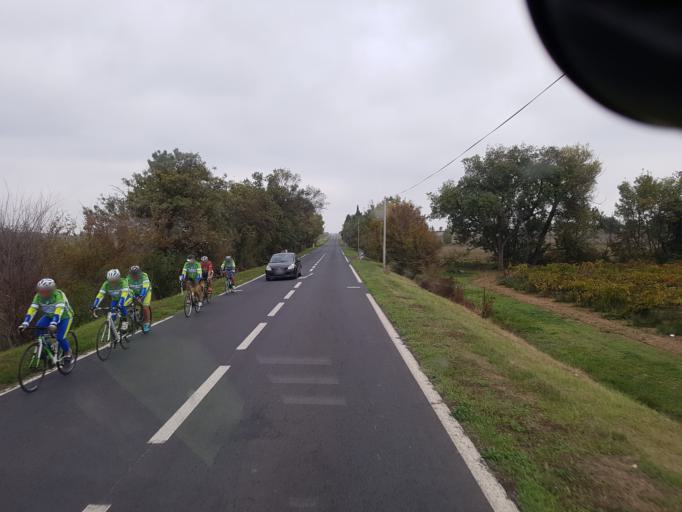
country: FR
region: Languedoc-Roussillon
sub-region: Departement de l'Herault
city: Pinet
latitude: 43.4051
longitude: 3.5407
